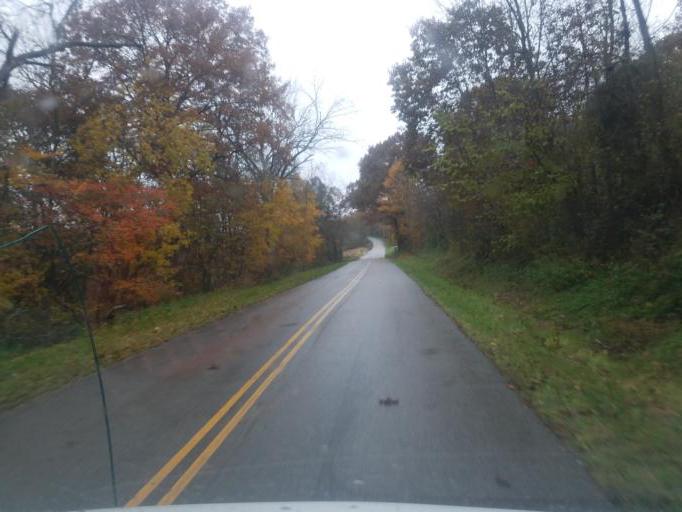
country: US
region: West Virginia
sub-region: Wood County
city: Vienna
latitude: 39.4239
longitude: -81.6136
